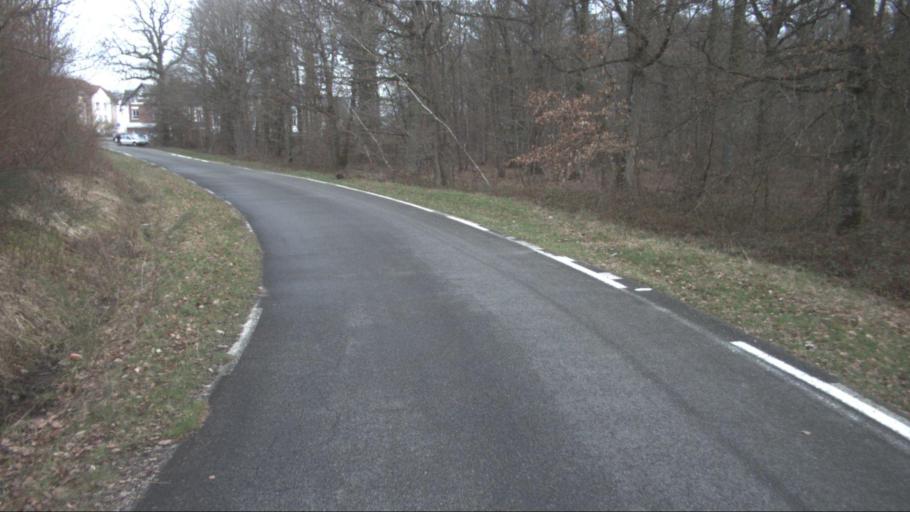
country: FR
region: Ile-de-France
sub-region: Departement des Yvelines
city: Le Perray-en-Yvelines
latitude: 48.6806
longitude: 1.8427
